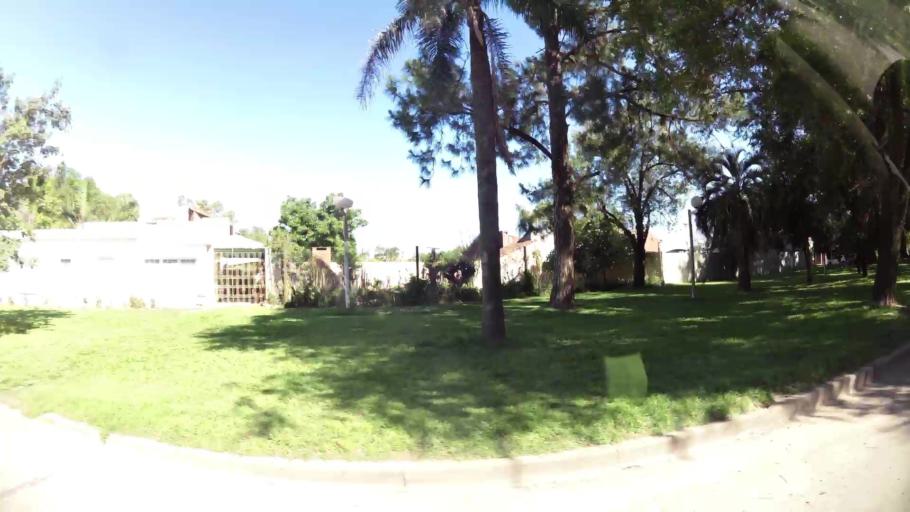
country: AR
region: Santa Fe
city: Esperanza
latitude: -31.4470
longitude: -60.9180
